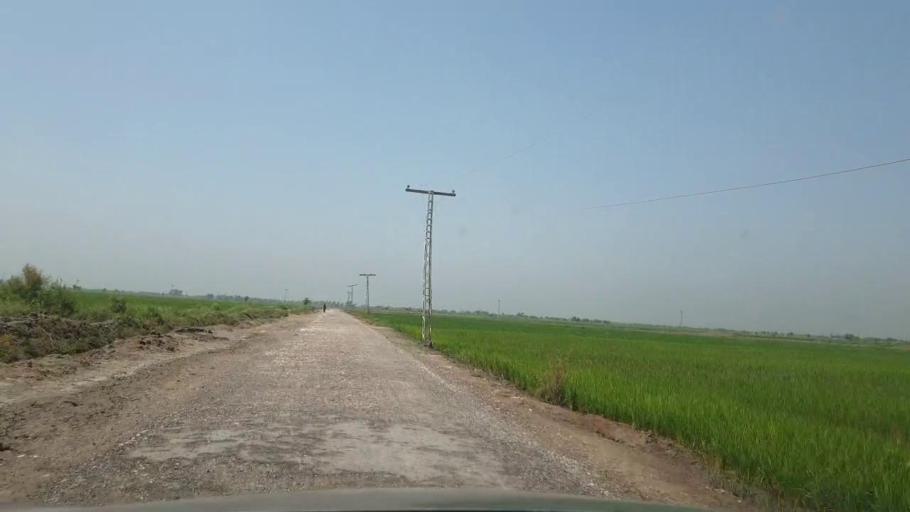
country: PK
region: Sindh
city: Warah
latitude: 27.4888
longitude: 67.7824
